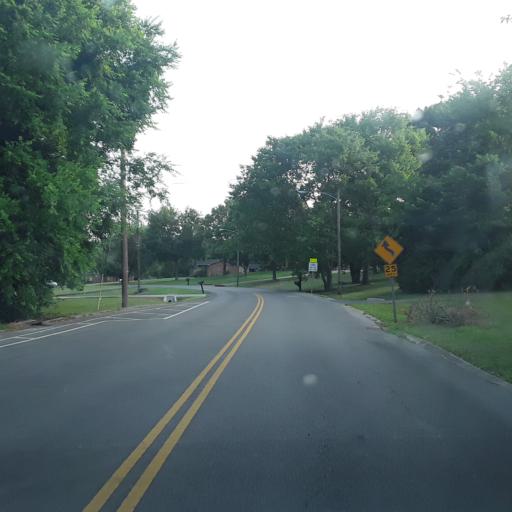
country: US
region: Tennessee
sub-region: Williamson County
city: Brentwood Estates
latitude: 36.0517
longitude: -86.7242
